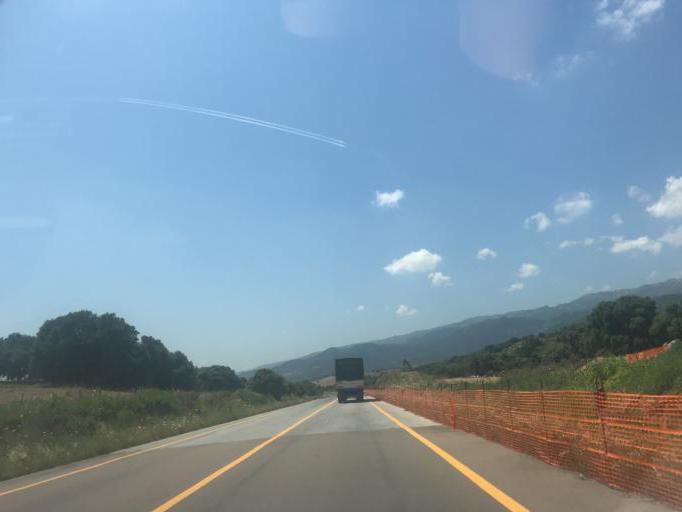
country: IT
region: Sardinia
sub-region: Provincia di Olbia-Tempio
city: Berchidda
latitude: 40.7805
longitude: 9.2252
